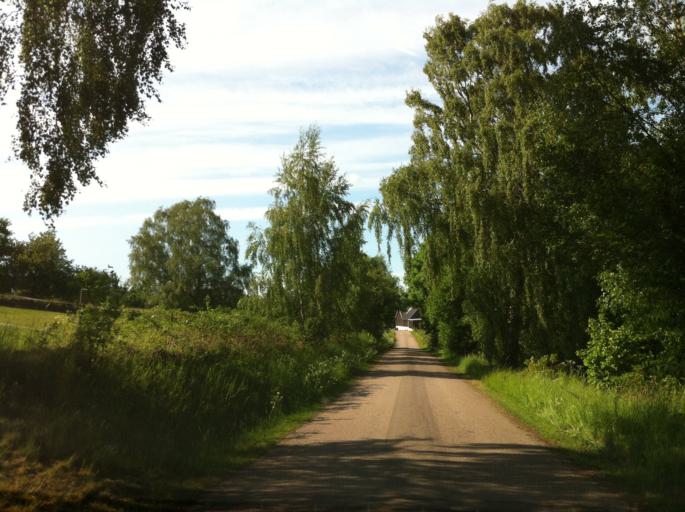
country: SE
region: Skane
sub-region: Klippans Kommun
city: Ljungbyhed
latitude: 56.0510
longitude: 13.2210
